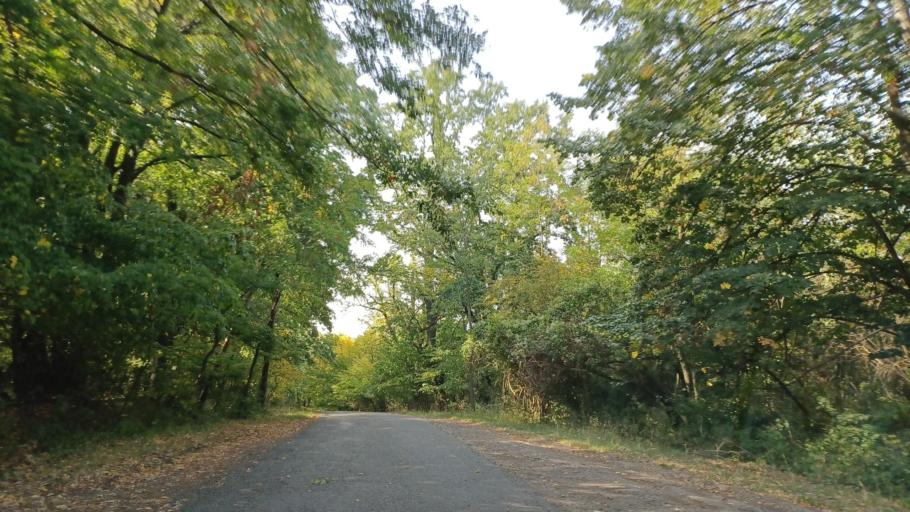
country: HU
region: Baranya
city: Mecseknadasd
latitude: 46.1952
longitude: 18.4501
